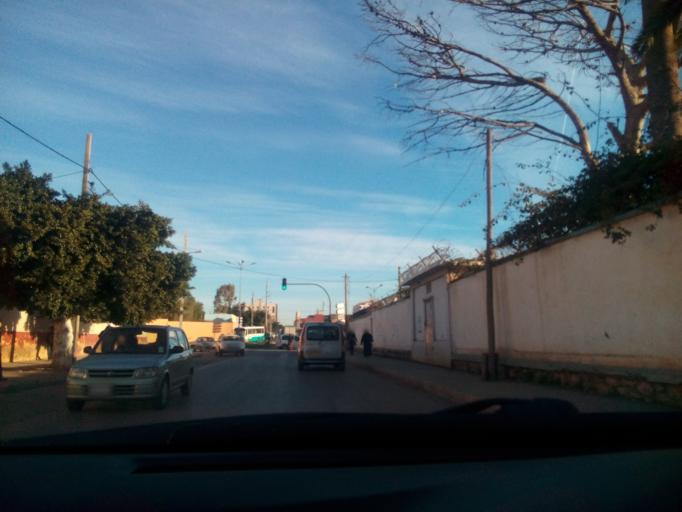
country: DZ
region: Oran
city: Oran
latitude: 35.6753
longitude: -0.6625
